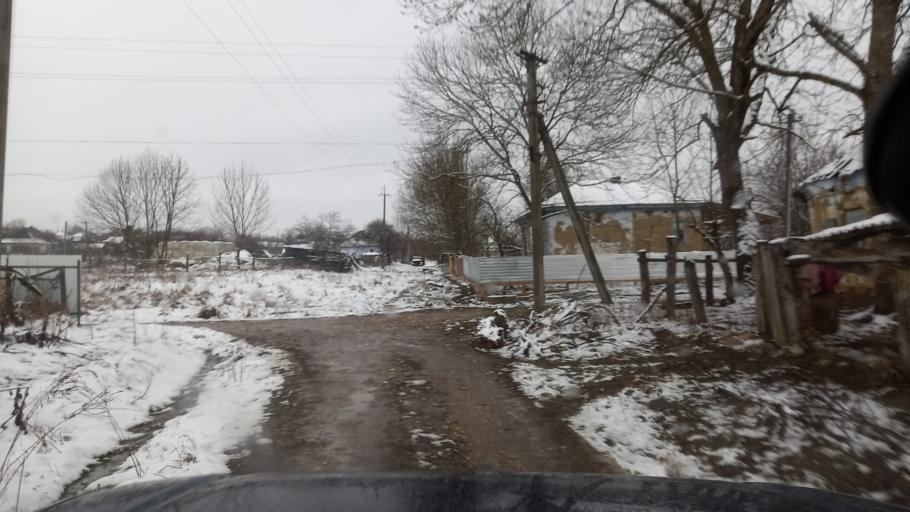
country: RU
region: Adygeya
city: Abadzekhskaya
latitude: 44.3560
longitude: 40.4146
